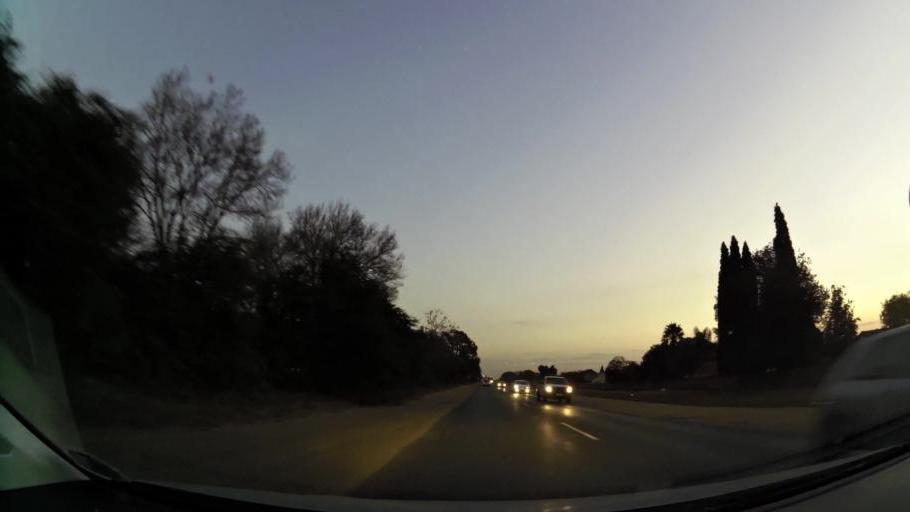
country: ZA
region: Gauteng
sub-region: Ekurhuleni Metropolitan Municipality
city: Tembisa
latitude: -26.0594
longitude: 28.2278
